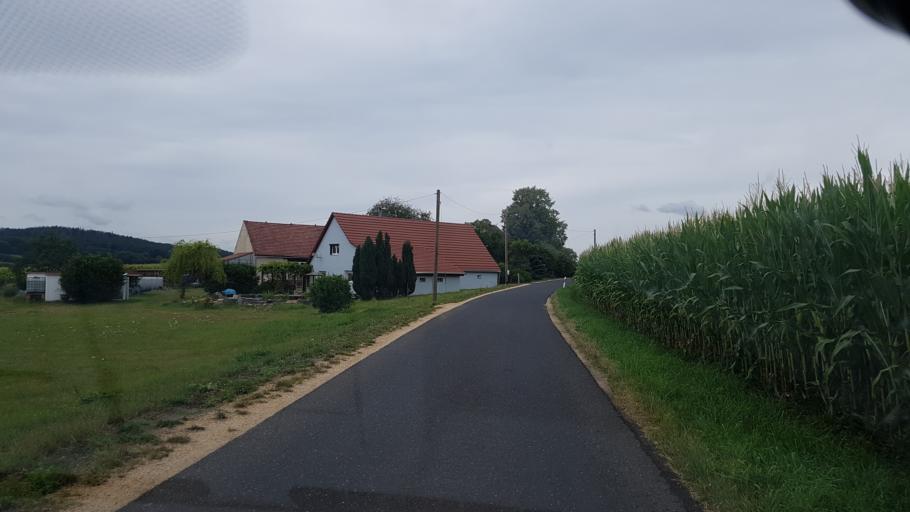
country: DE
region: Saxony
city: Kodersdorf
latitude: 51.2255
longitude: 14.8759
